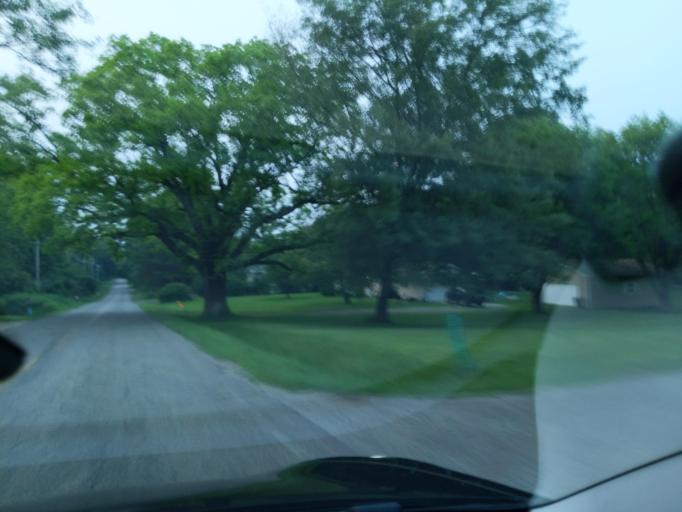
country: US
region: Michigan
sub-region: Ingham County
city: Leslie
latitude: 42.3625
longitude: -84.4925
